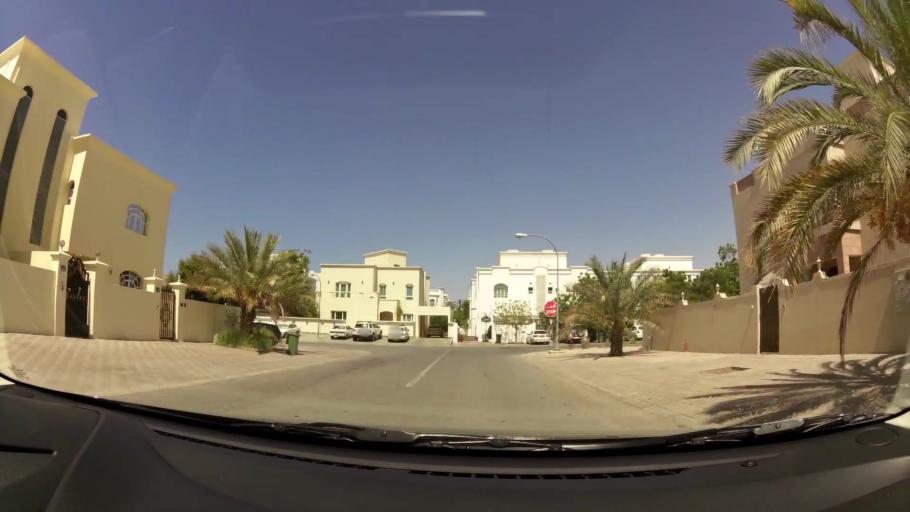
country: OM
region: Muhafazat Masqat
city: Bawshar
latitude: 23.6014
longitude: 58.3636
